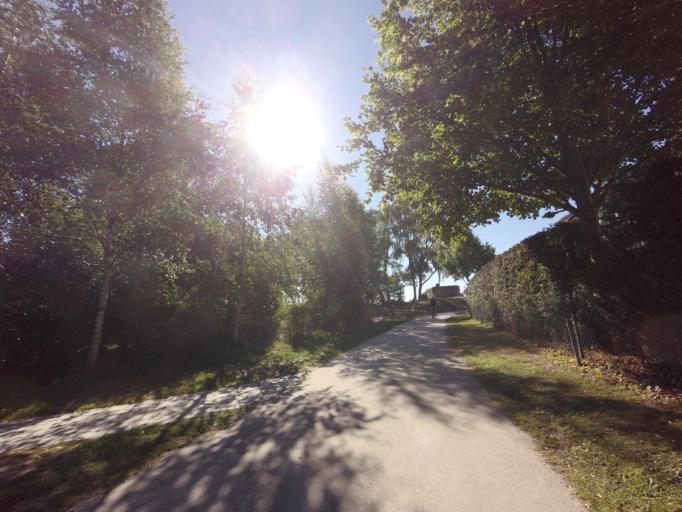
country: SE
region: Skane
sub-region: Ystads Kommun
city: Ystad
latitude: 55.4260
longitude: 13.8501
